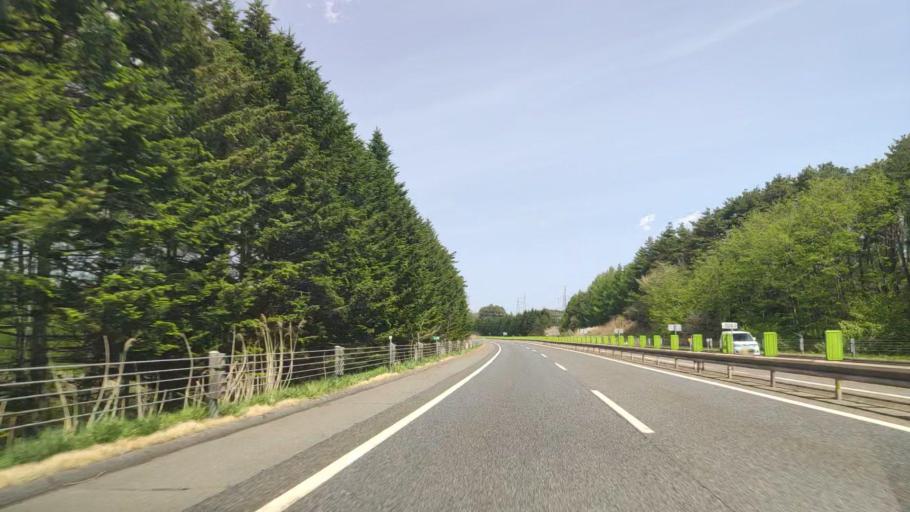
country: JP
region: Aomori
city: Hachinohe
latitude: 40.4366
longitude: 141.4467
